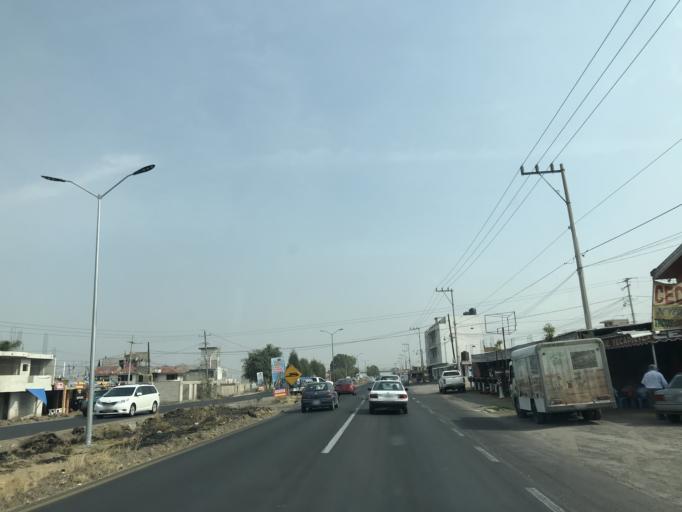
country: MX
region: Tlaxcala
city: Tenancingo
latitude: 19.1441
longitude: -98.1916
